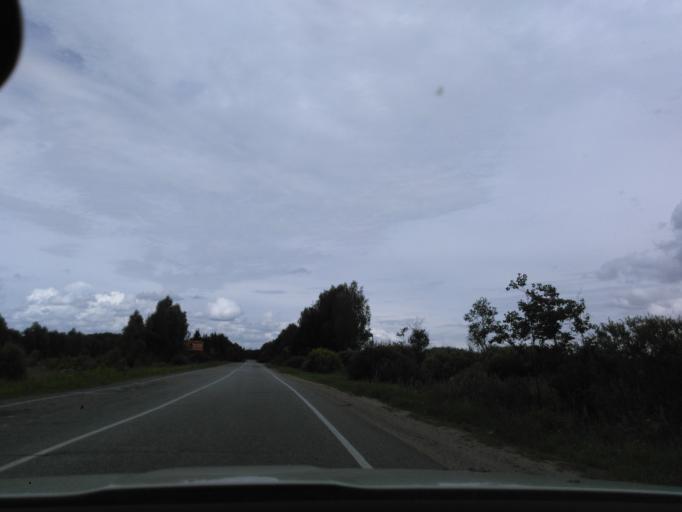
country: RU
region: Tverskaya
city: Konakovo
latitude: 56.6564
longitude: 36.7145
